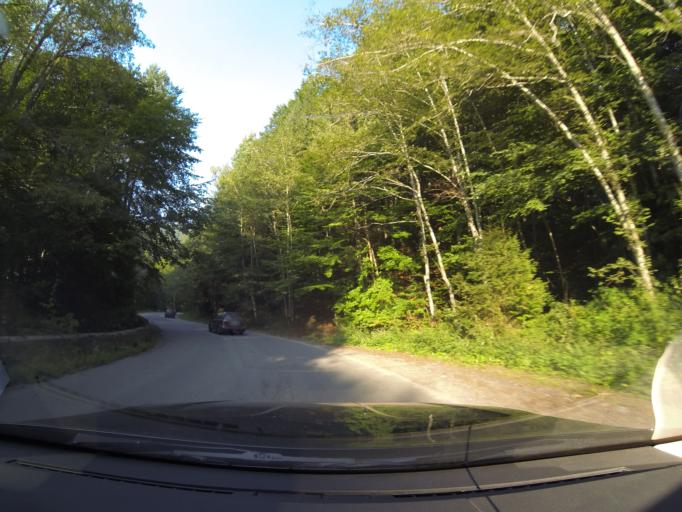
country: RO
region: Arges
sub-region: Comuna Arefu
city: Arefu
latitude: 45.4029
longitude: 24.6440
